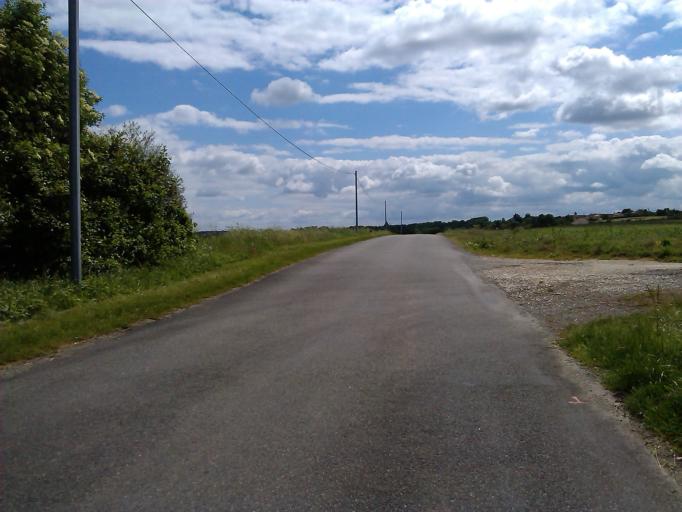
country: FR
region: Poitou-Charentes
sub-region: Departement de la Charente
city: Mansle
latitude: 45.9299
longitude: 0.2352
